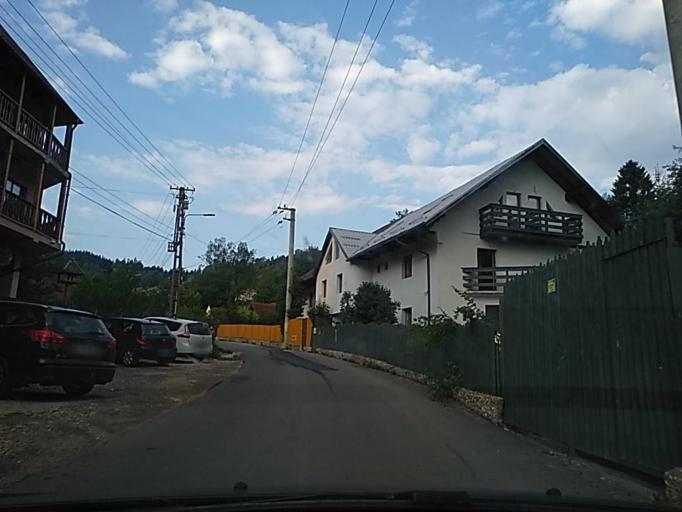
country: RO
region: Brasov
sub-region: Comuna Bran
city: Simon
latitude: 45.4941
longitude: 25.3842
